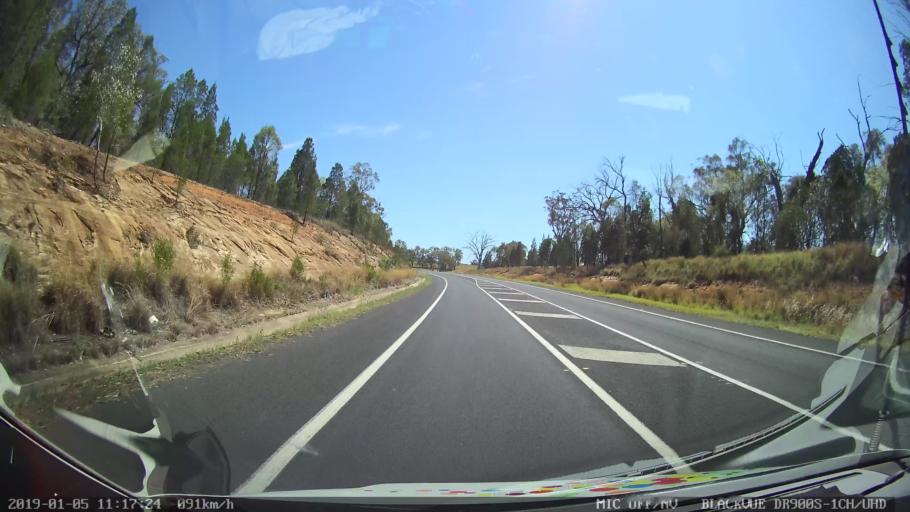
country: AU
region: New South Wales
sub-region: Warrumbungle Shire
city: Coonabarabran
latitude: -31.3271
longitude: 149.3069
